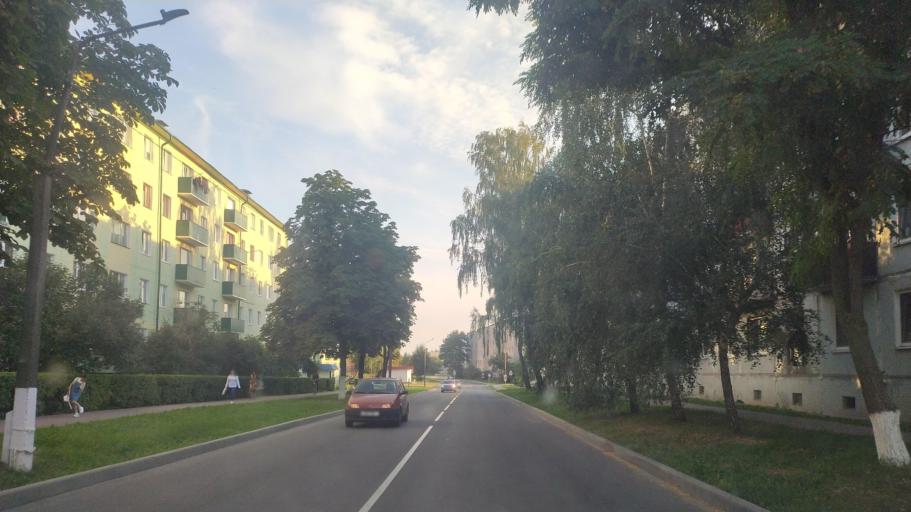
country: BY
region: Brest
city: Byaroza
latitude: 52.5415
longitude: 24.9843
